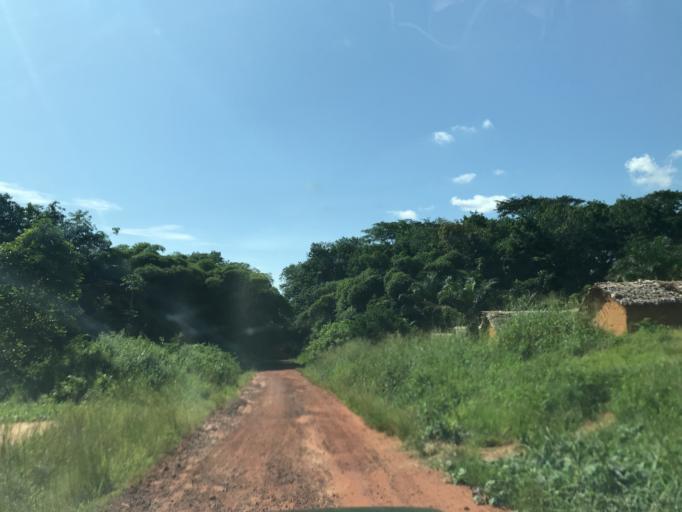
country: CD
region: Eastern Province
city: Kisangani
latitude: 1.2664
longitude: 25.2796
